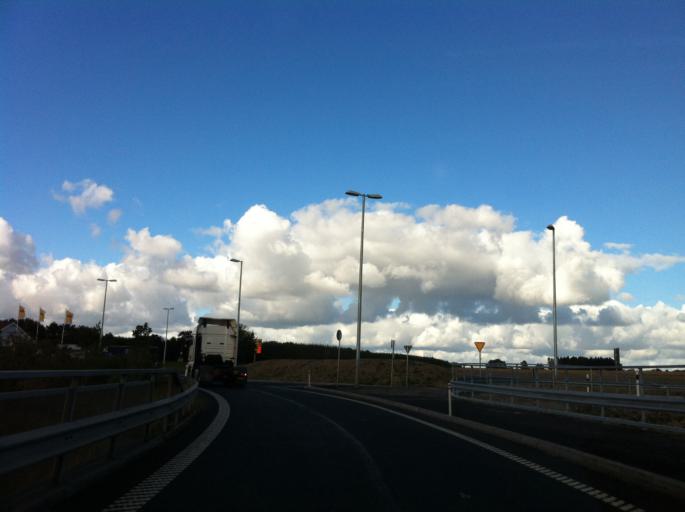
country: SE
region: Skane
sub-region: Eslovs Kommun
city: Eslov
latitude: 55.7685
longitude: 13.3213
